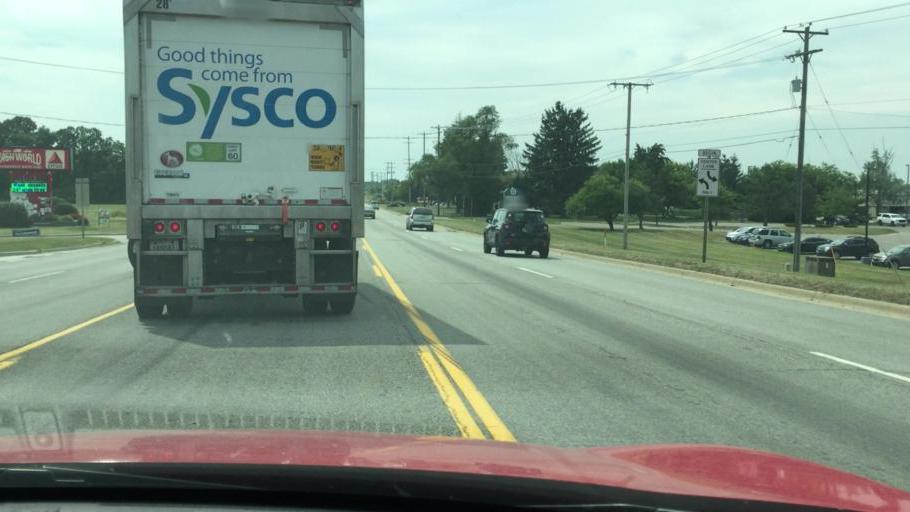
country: US
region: Michigan
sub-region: Genesee County
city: Flint
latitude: 42.9442
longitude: -83.7153
